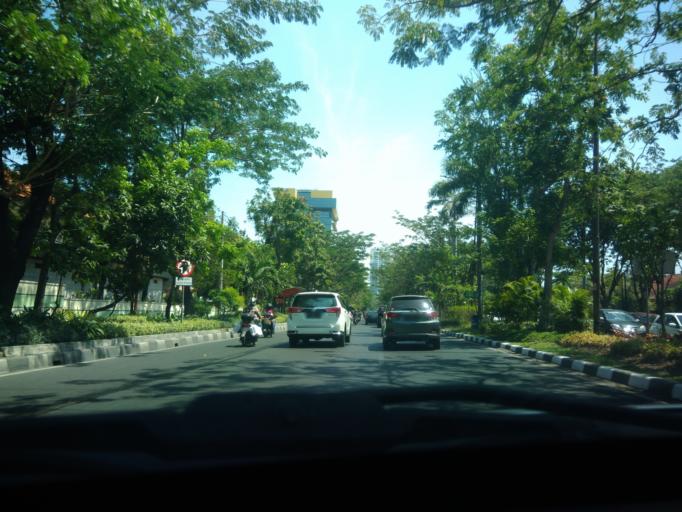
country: ID
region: East Java
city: Semampir
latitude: -7.2891
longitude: 112.7806
